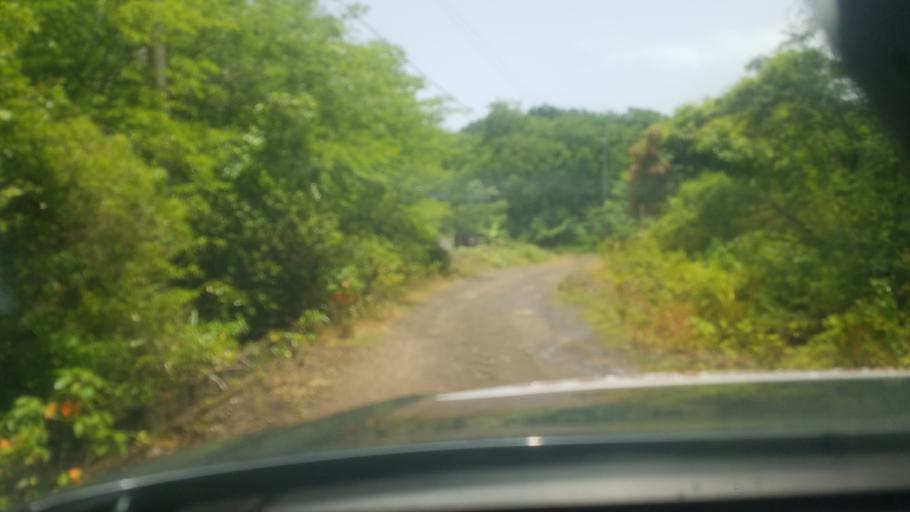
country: LC
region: Gros-Islet
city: Gros Islet
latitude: 14.0520
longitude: -60.9350
